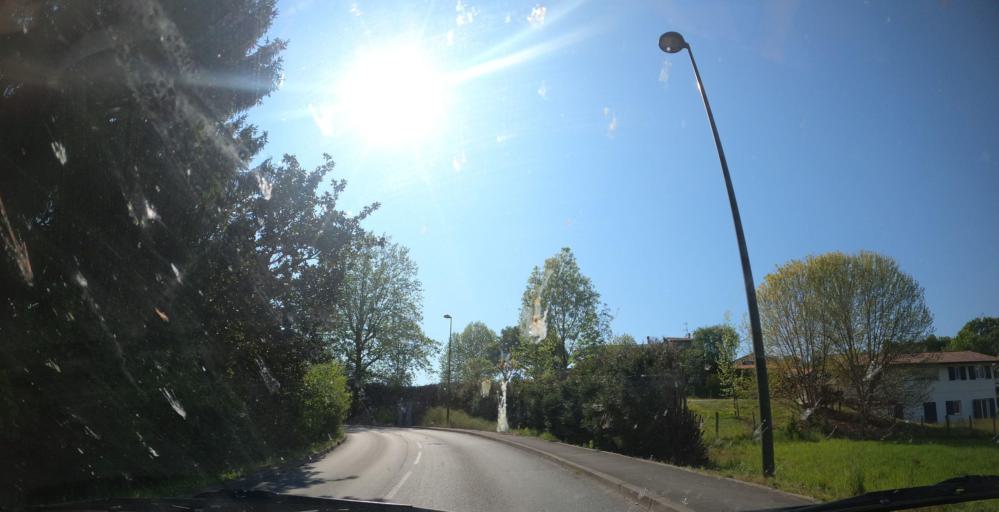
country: FR
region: Aquitaine
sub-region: Departement des Pyrenees-Atlantiques
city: Bassussarry
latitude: 43.4457
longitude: -1.5069
